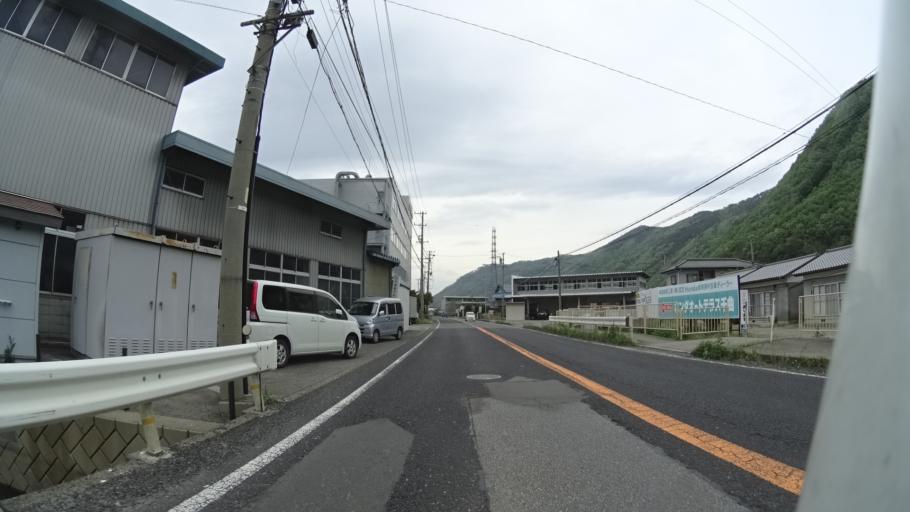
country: JP
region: Nagano
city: Nagano-shi
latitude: 36.4960
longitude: 138.1498
